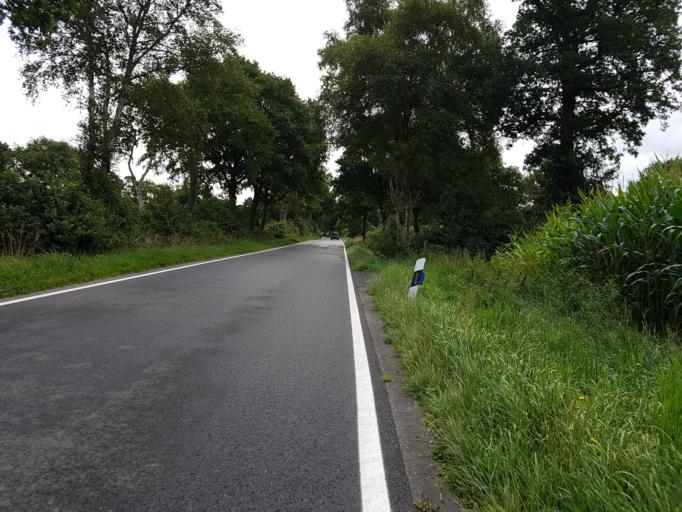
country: DE
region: Lower Saxony
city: Wittmund
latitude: 53.5236
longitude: 7.7198
